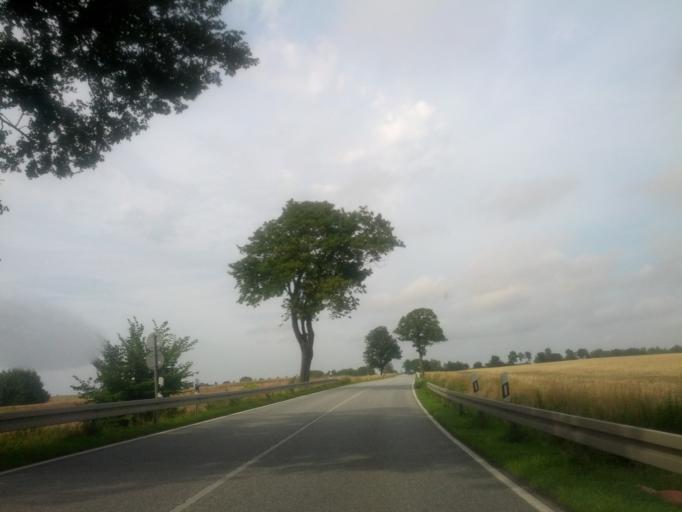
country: DE
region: Mecklenburg-Vorpommern
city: Sellin
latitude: 53.9625
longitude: 11.6160
